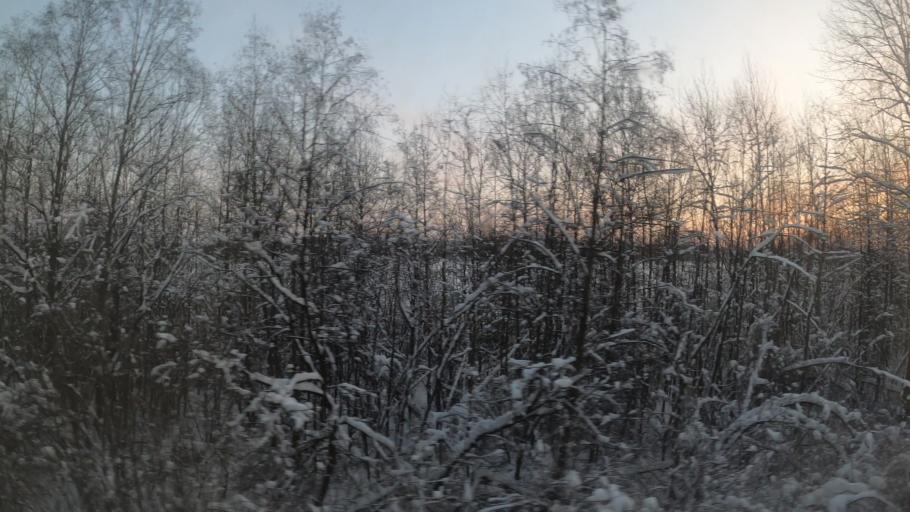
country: RU
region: Moskovskaya
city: Yermolino
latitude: 56.1493
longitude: 37.5054
